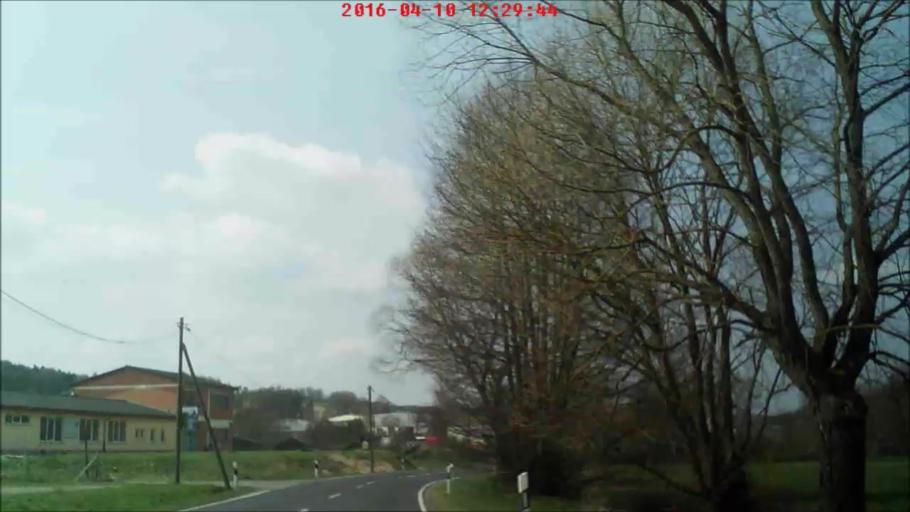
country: DE
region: Thuringia
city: Springstille
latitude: 50.6877
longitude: 10.5188
